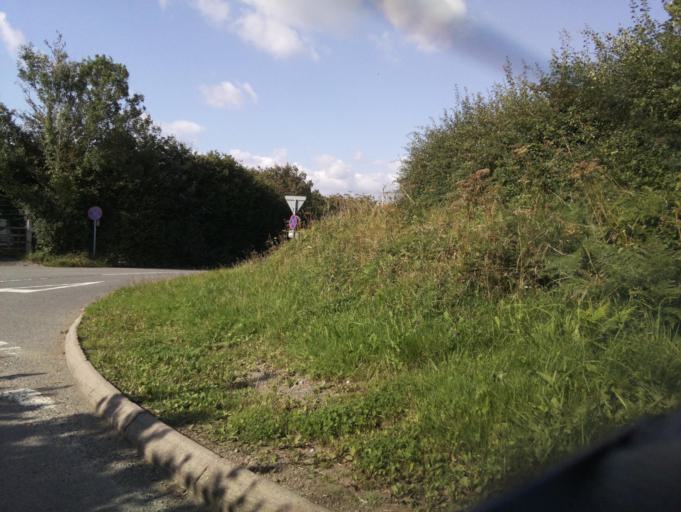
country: GB
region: England
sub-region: Devon
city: Buckfastleigh
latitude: 50.4455
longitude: -3.7936
